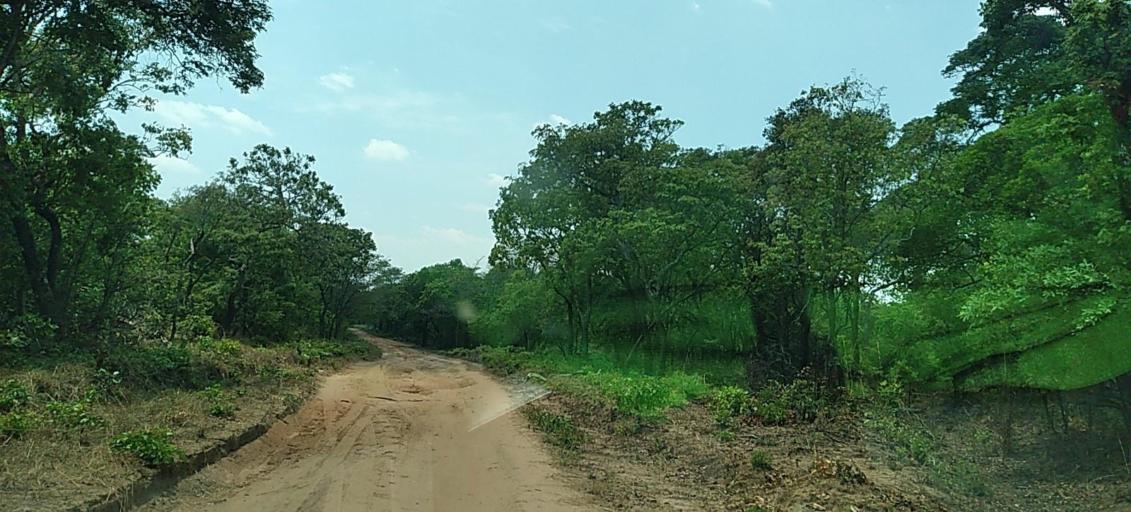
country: CD
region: Katanga
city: Kolwezi
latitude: -11.3505
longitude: 25.2138
